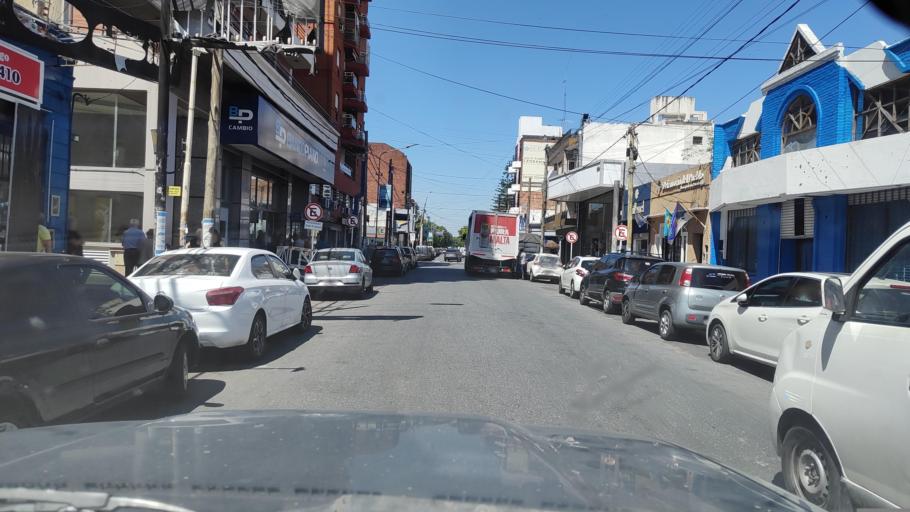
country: AR
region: Buenos Aires
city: San Justo
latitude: -34.6793
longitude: -58.5619
